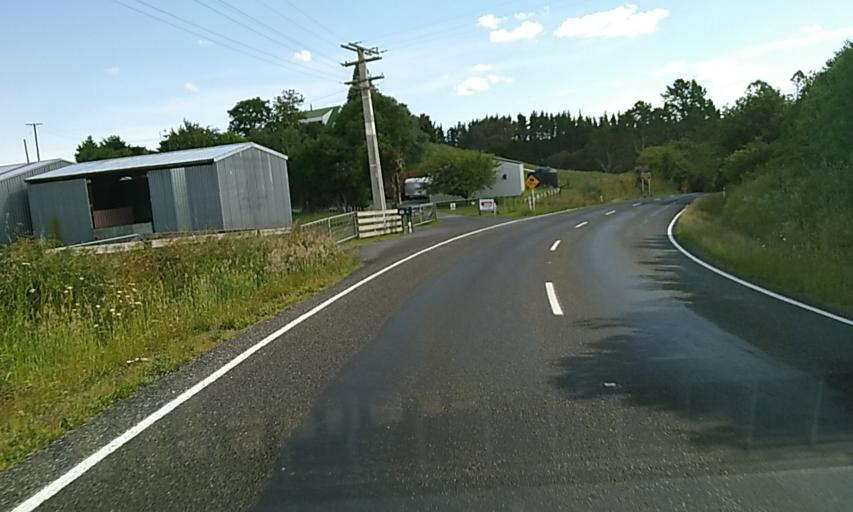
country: NZ
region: Bay of Plenty
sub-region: Tauranga City
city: Tauranga
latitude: -37.8029
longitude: 176.0435
